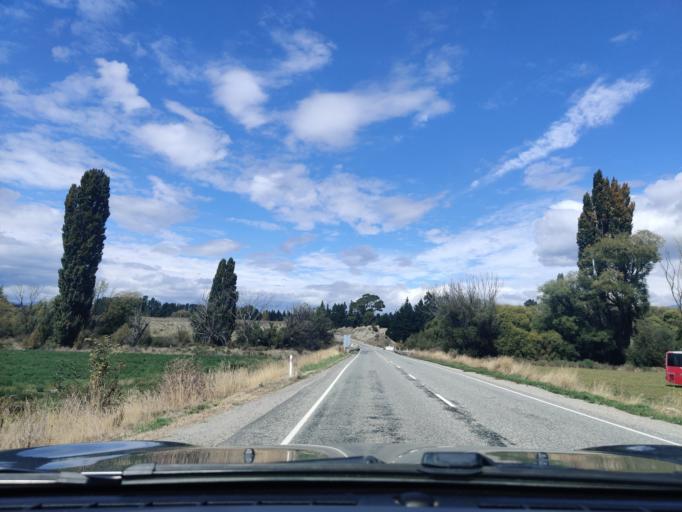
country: NZ
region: Otago
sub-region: Queenstown-Lakes District
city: Wanaka
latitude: -44.6981
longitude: 169.1763
